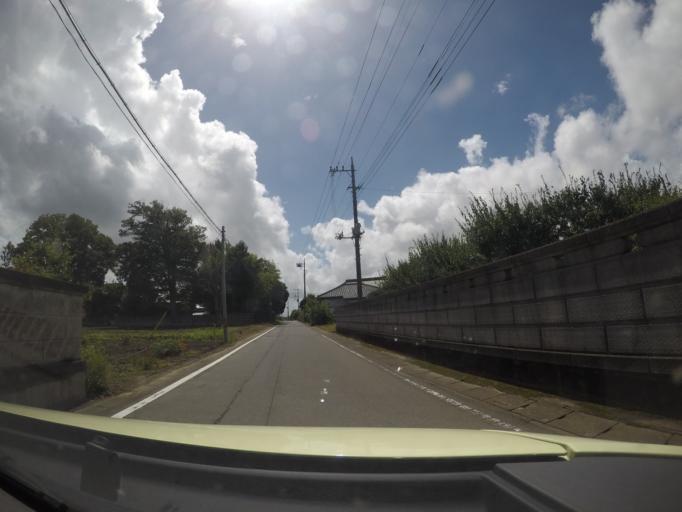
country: JP
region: Ibaraki
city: Mitsukaido
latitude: 36.0606
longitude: 140.0067
